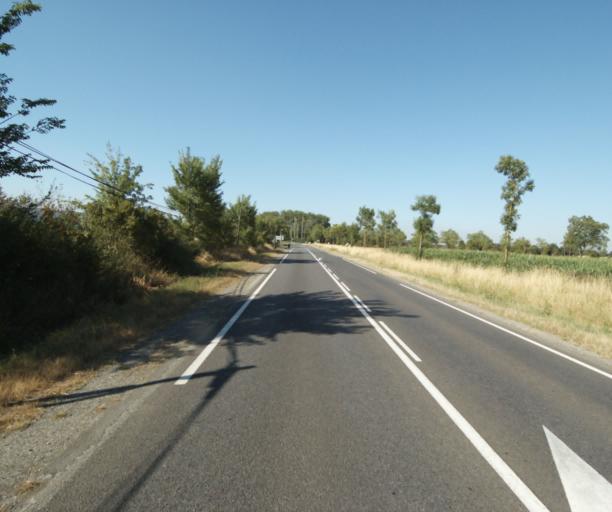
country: FR
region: Midi-Pyrenees
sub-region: Departement de la Haute-Garonne
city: Revel
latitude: 43.4784
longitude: 2.0184
